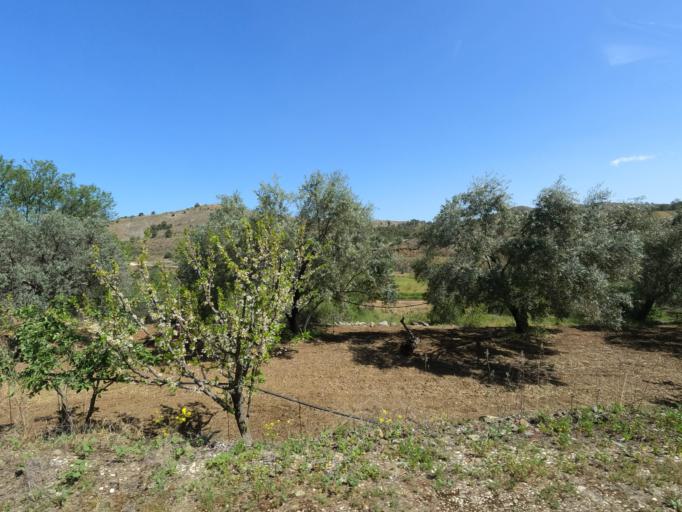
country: CY
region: Lefkosia
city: Astromeritis
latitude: 35.0624
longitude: 33.0218
